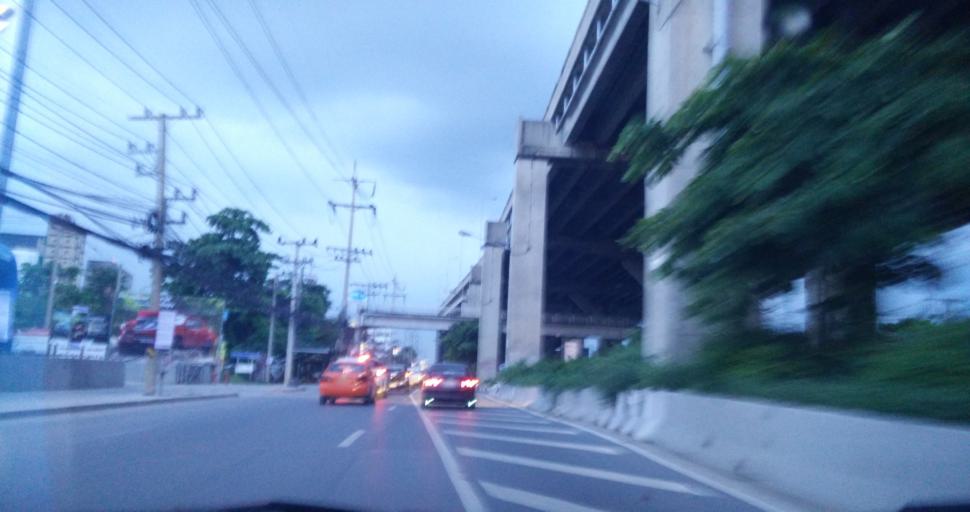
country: TH
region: Phra Nakhon Si Ayutthaya
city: Ban Bang Kadi Pathum Thani
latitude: 13.9996
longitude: 100.6147
